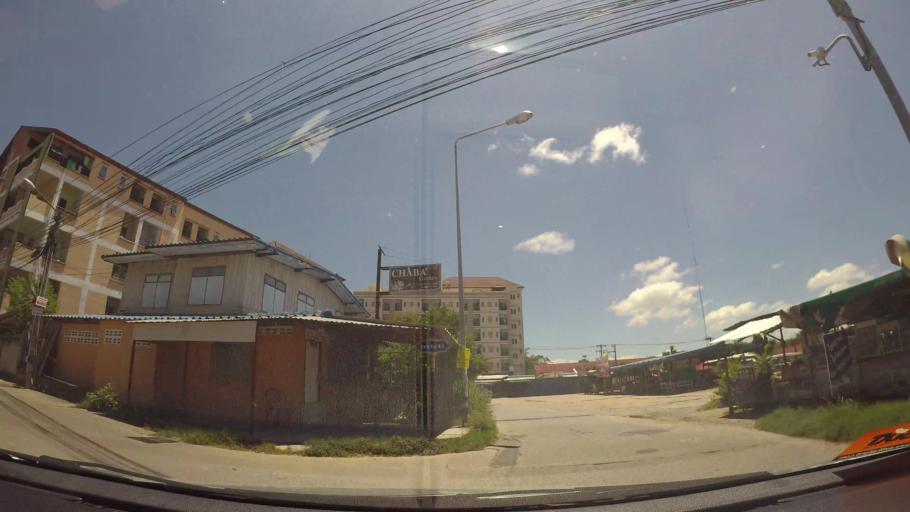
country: TH
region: Chon Buri
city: Phatthaya
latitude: 12.9240
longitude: 100.8915
